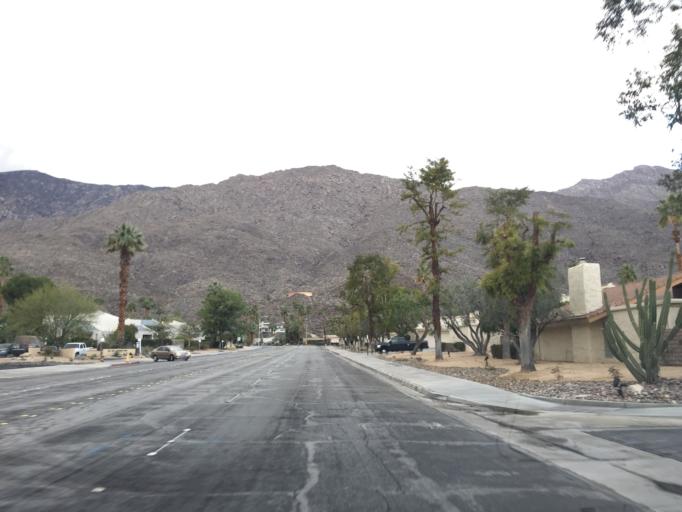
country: US
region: California
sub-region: Riverside County
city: Palm Springs
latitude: 33.7941
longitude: -116.5434
